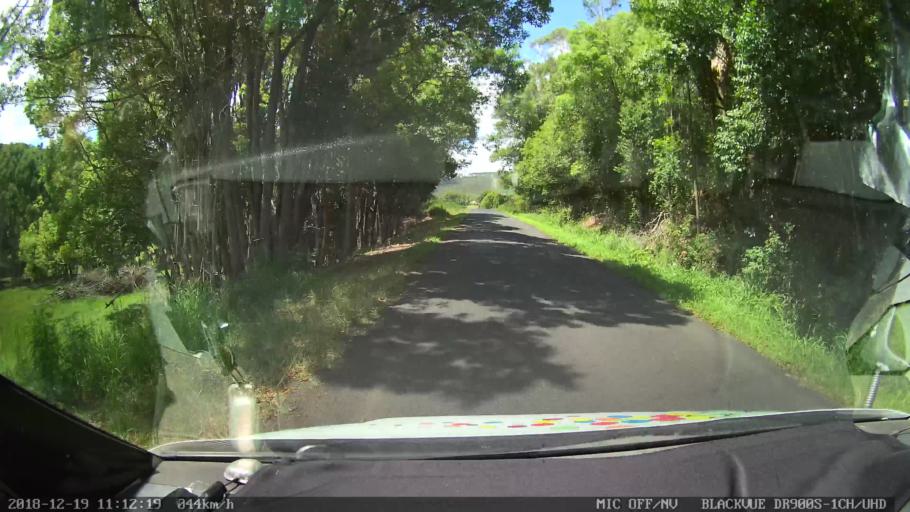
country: AU
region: New South Wales
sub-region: Lismore Municipality
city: Nimbin
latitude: -28.6480
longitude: 153.2606
